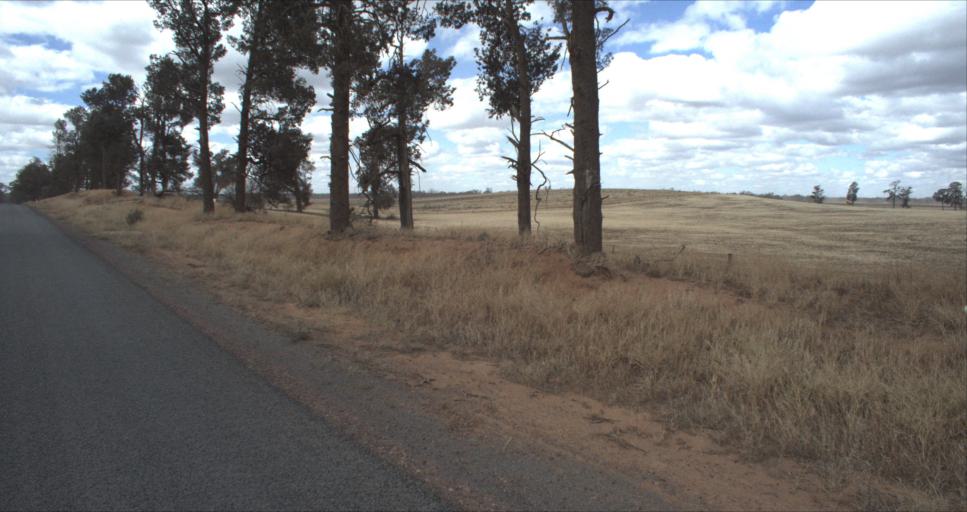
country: AU
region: New South Wales
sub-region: Leeton
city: Leeton
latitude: -34.6602
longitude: 146.3495
